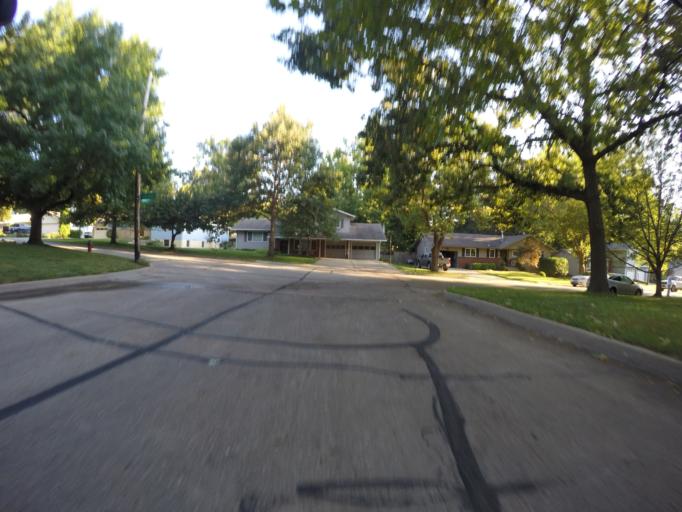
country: US
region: Kansas
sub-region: Riley County
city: Manhattan
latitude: 39.1996
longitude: -96.6095
